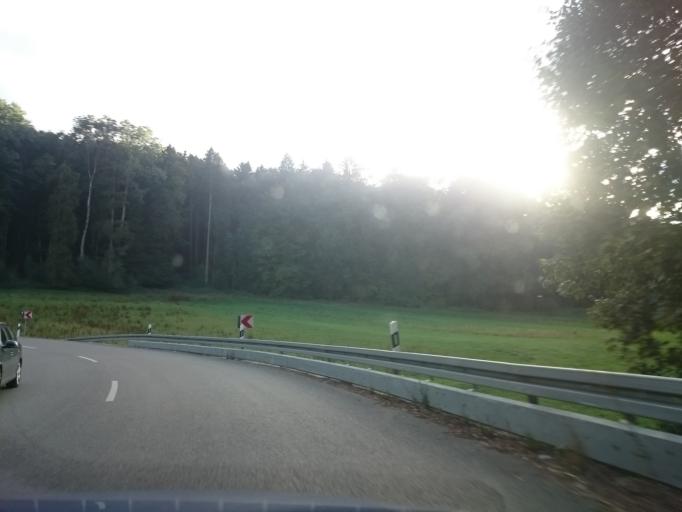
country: DE
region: Bavaria
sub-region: Regierungsbezirk Mittelfranken
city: Thalmassing
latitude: 49.0784
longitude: 11.1961
